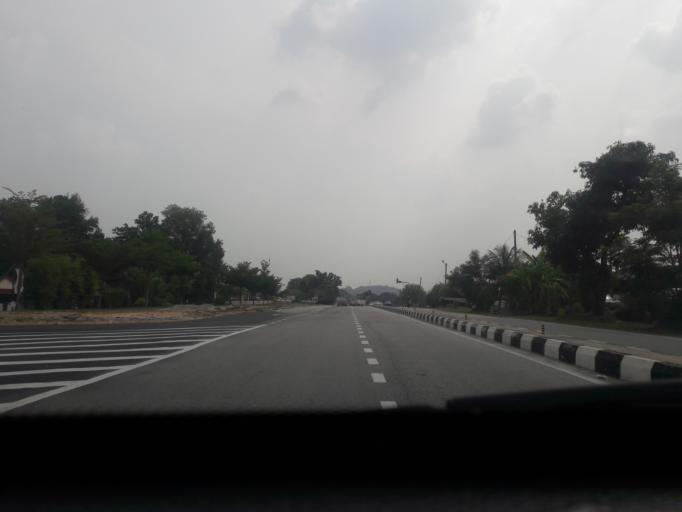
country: MY
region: Kedah
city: Kulim
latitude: 5.3717
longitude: 100.5341
